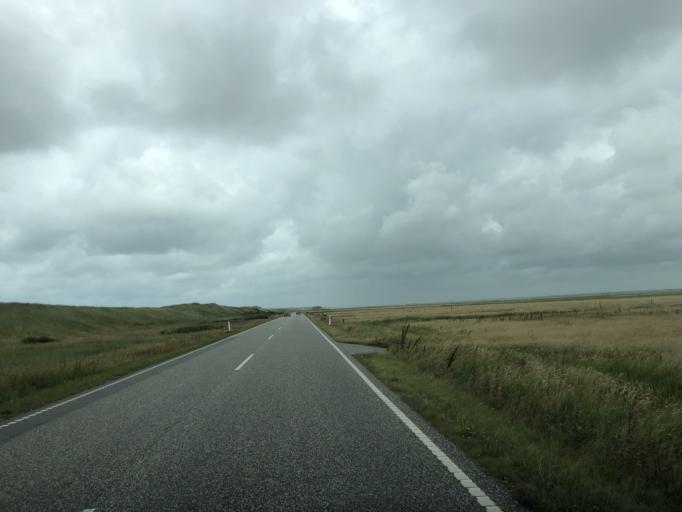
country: DK
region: Central Jutland
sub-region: Holstebro Kommune
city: Ulfborg
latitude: 56.3880
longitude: 8.1218
